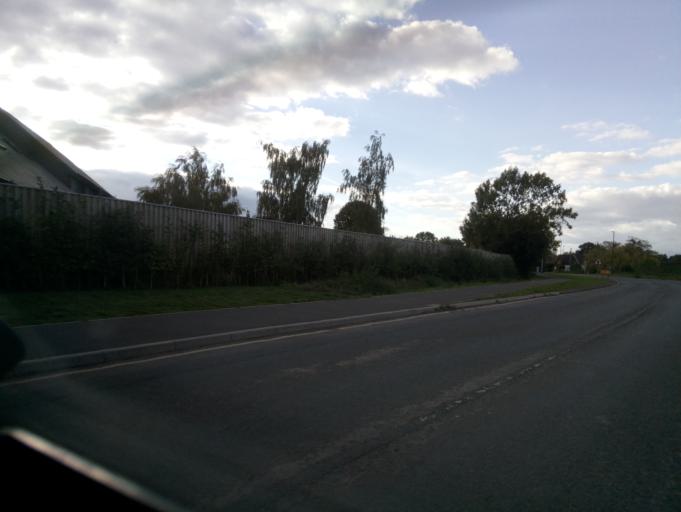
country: GB
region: England
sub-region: Herefordshire
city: Withington
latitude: 52.0683
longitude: -2.6342
